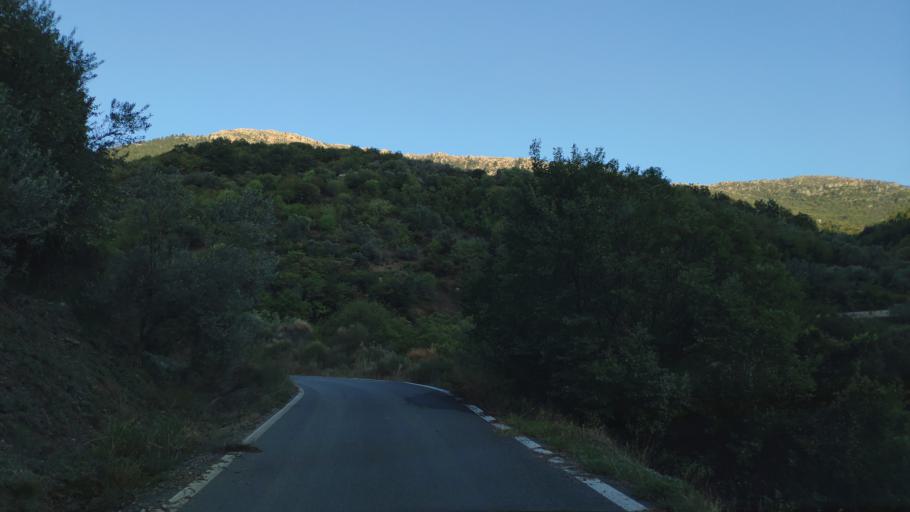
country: GR
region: Peloponnese
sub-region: Nomos Arkadias
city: Dimitsana
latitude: 37.5669
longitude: 22.0463
